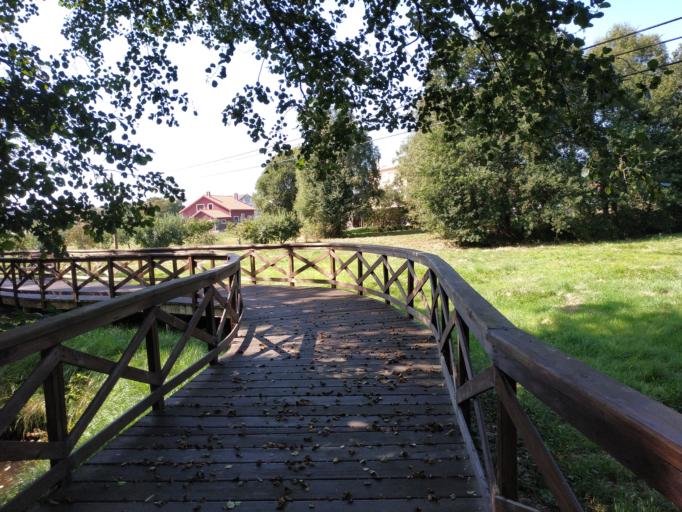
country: ES
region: Galicia
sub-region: Provincia da Coruna
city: Laracha
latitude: 43.2509
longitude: -8.6103
